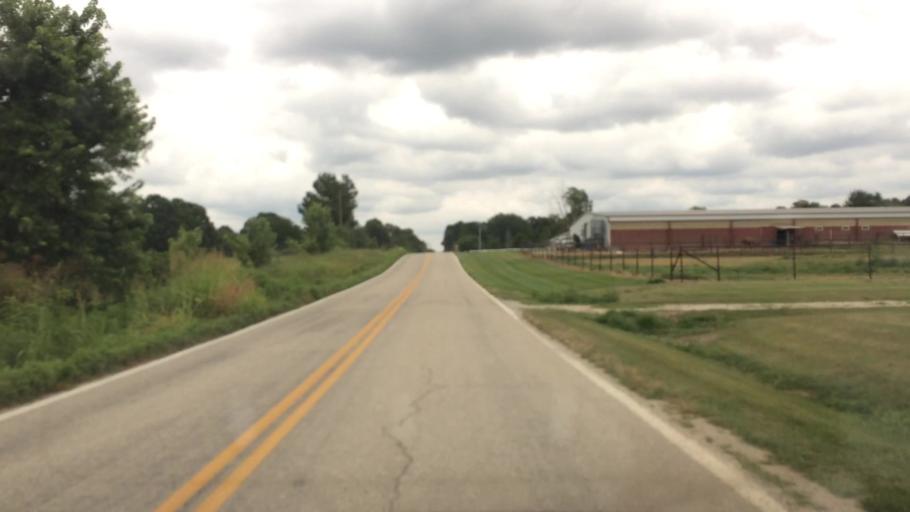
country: US
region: Missouri
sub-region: Greene County
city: Strafford
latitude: 37.3005
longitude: -93.1628
